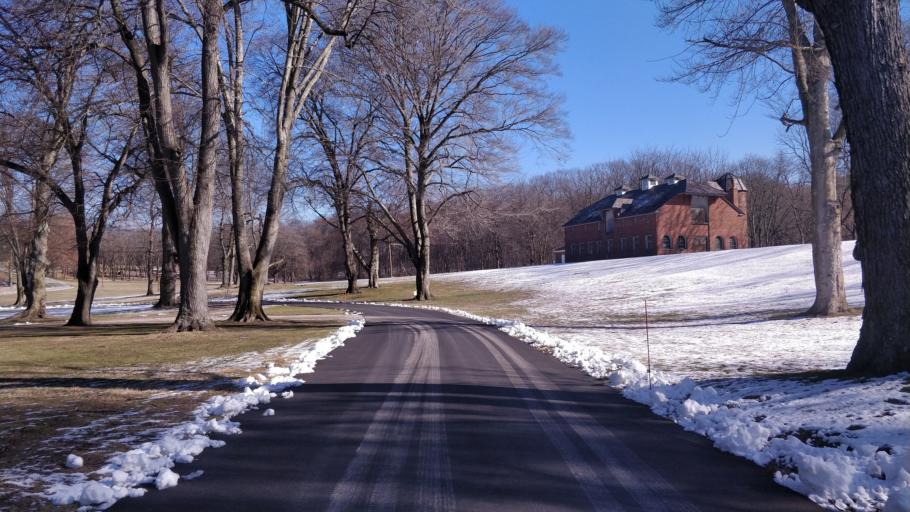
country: US
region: New York
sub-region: Nassau County
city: Old Westbury
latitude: 40.7848
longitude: -73.5877
